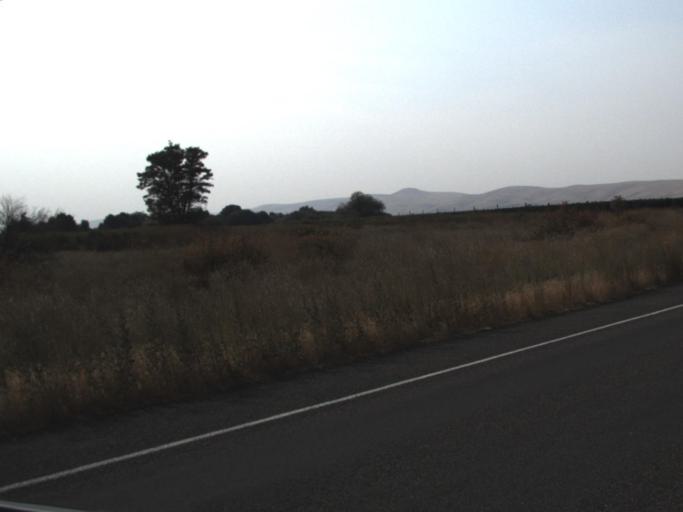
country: US
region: Washington
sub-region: Yakima County
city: Granger
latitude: 46.2810
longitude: -120.1660
